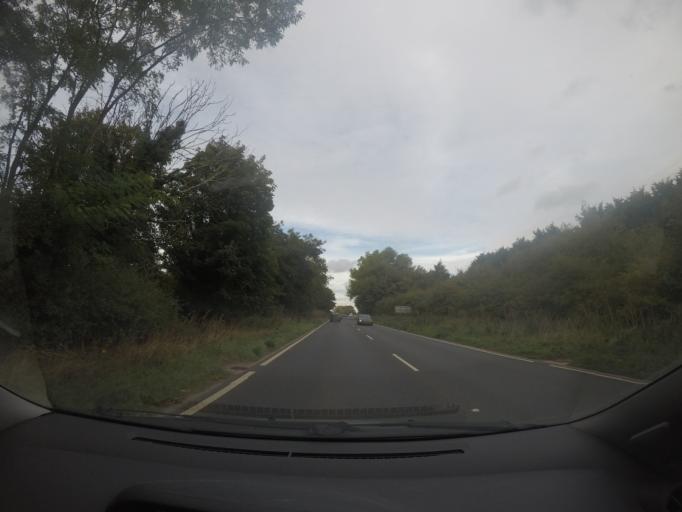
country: GB
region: England
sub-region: City of York
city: Deighton
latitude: 53.8973
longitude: -1.0475
